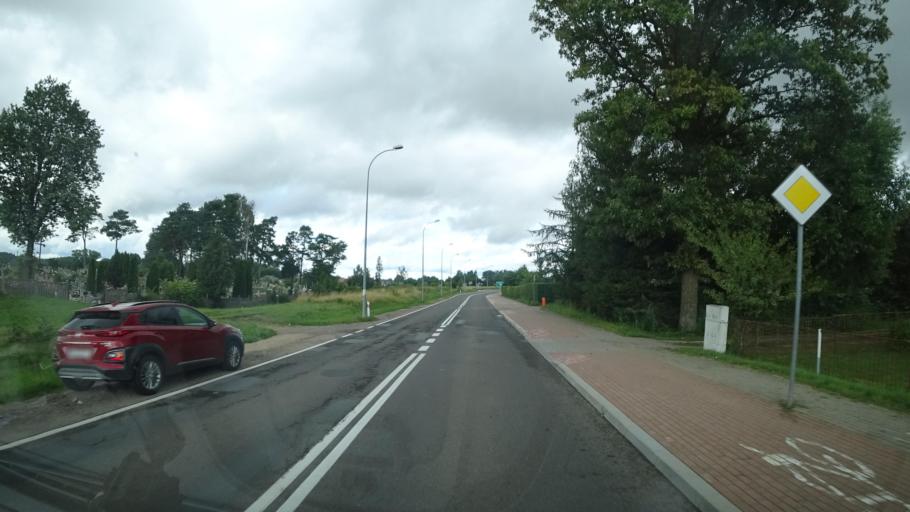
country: PL
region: Warmian-Masurian Voivodeship
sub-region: Powiat olecki
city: Kowale Oleckie
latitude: 54.1726
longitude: 22.4148
